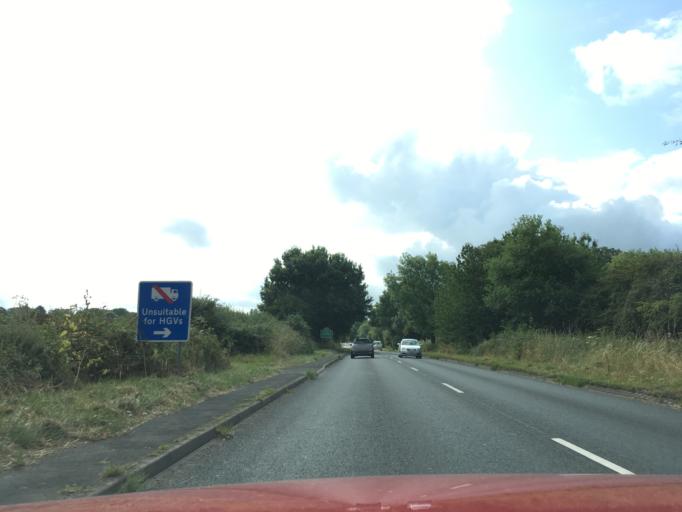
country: GB
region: England
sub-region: Hampshire
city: Bishops Waltham
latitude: 50.9626
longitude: -1.2362
